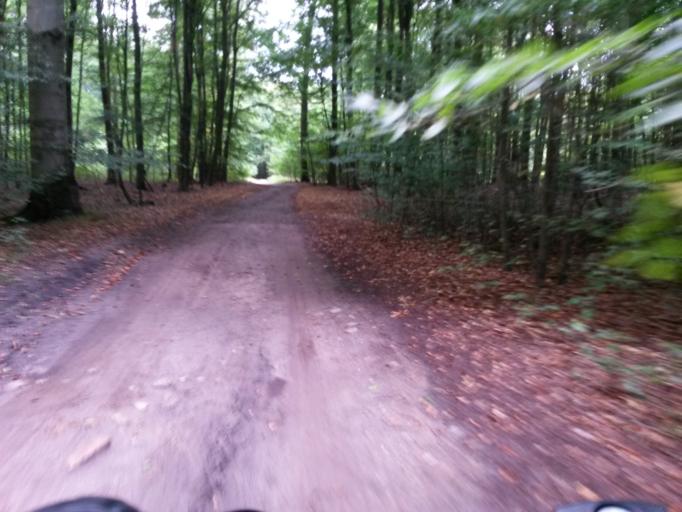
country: DE
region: Brandenburg
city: Templin
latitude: 53.0885
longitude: 13.5453
